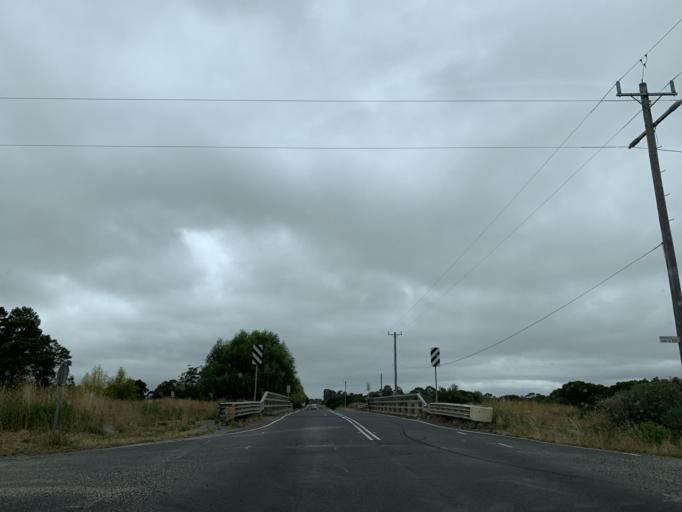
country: AU
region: Victoria
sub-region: Cardinia
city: Pakenham South
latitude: -38.1560
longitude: 145.5029
